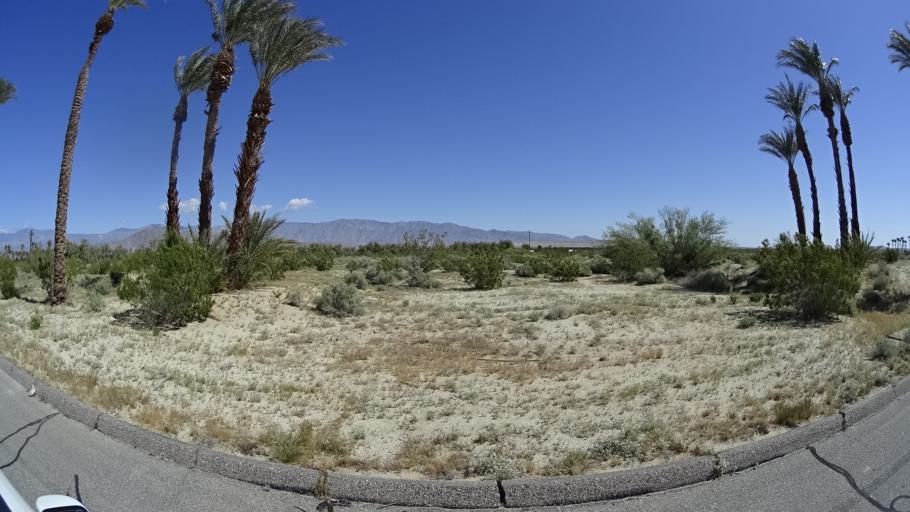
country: US
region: California
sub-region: San Diego County
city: Borrego Springs
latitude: 33.2332
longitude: -116.3515
